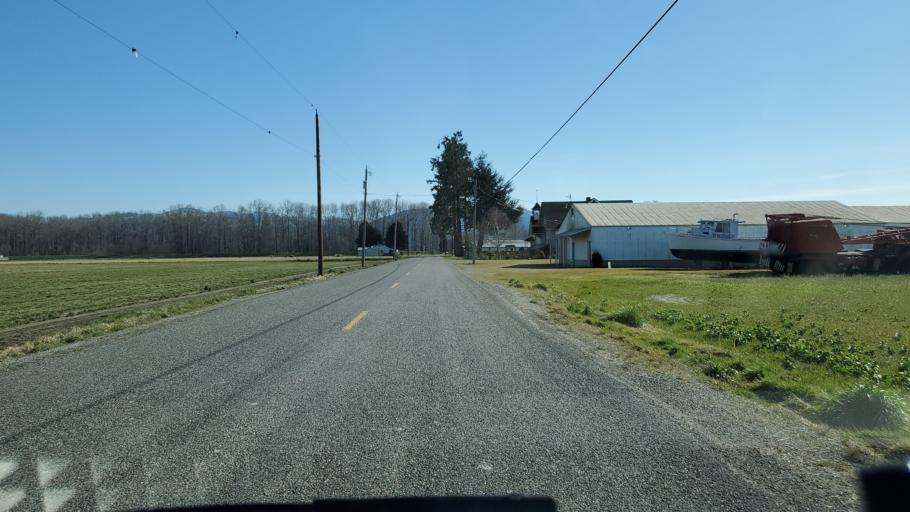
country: US
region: Washington
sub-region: Skagit County
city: Mount Vernon
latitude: 48.3702
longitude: -122.3698
